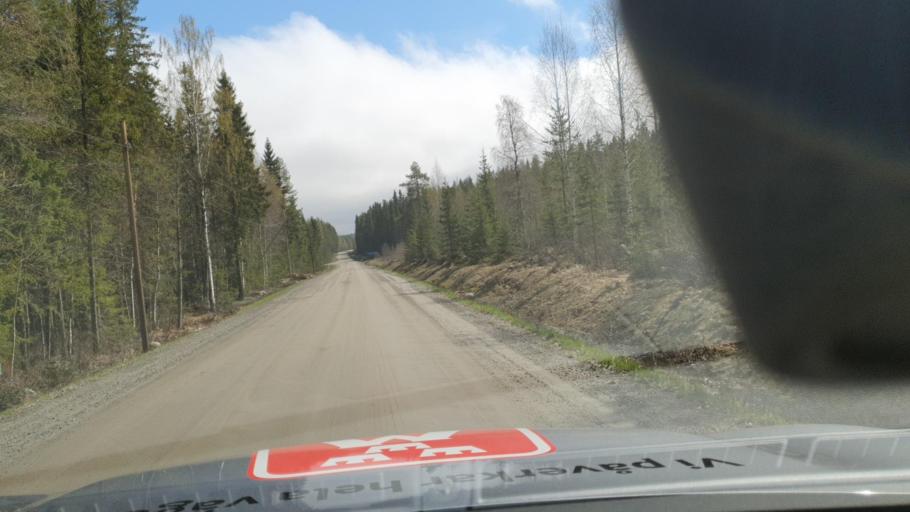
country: SE
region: Vaesterbotten
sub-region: Bjurholms Kommun
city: Bjurholm
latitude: 63.6811
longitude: 18.9843
